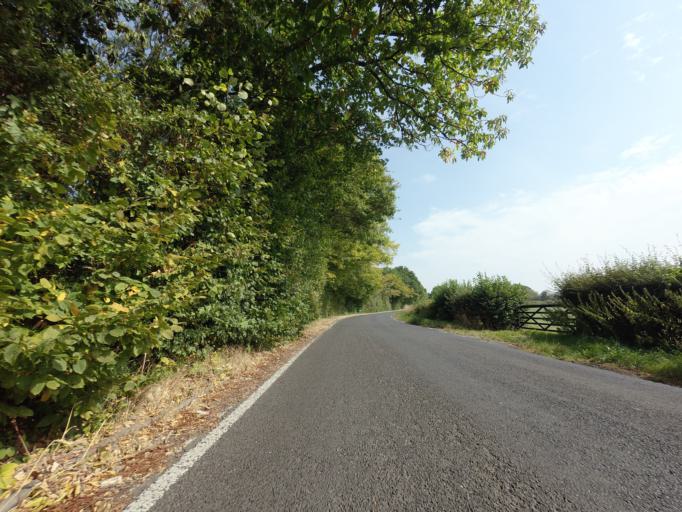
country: GB
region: England
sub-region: Kent
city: Staplehurst
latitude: 51.1341
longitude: 0.5816
